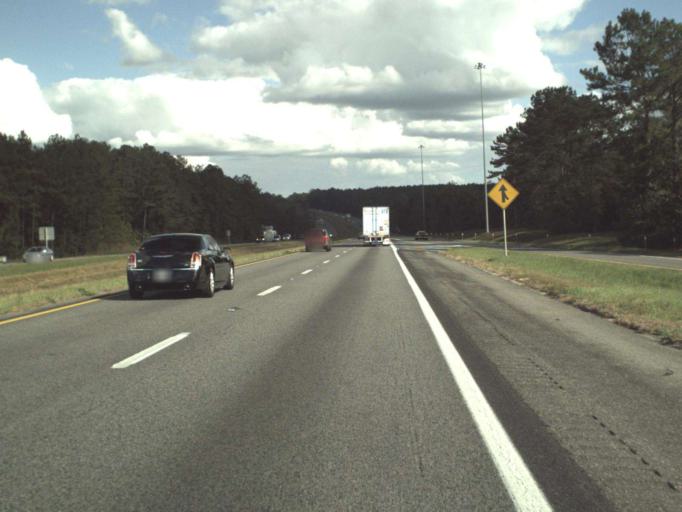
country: US
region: Florida
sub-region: Jefferson County
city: Monticello
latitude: 30.4749
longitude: -83.8871
